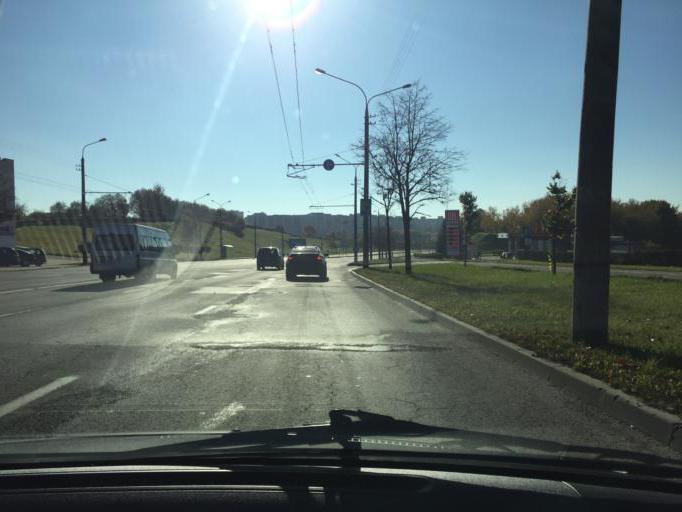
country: BY
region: Minsk
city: Syenitsa
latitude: 53.8601
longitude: 27.5372
